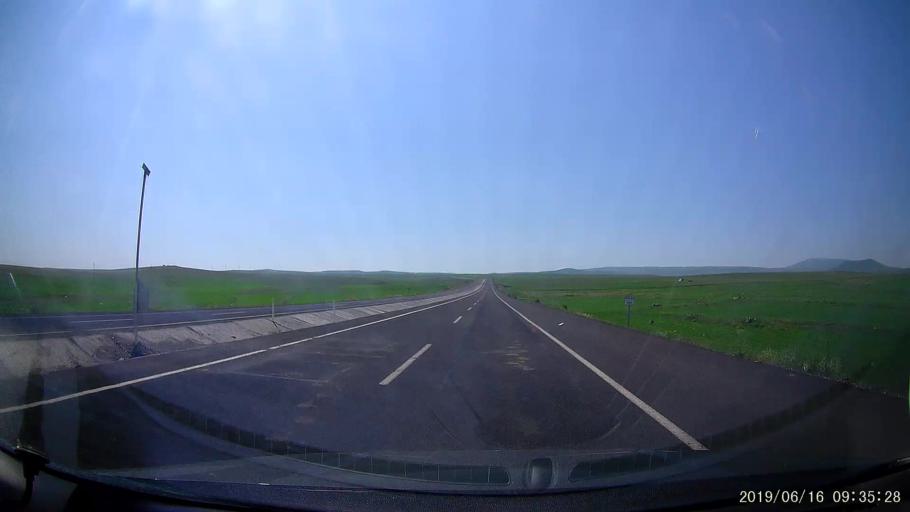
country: TR
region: Kars
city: Kars
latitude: 40.5715
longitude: 43.1564
